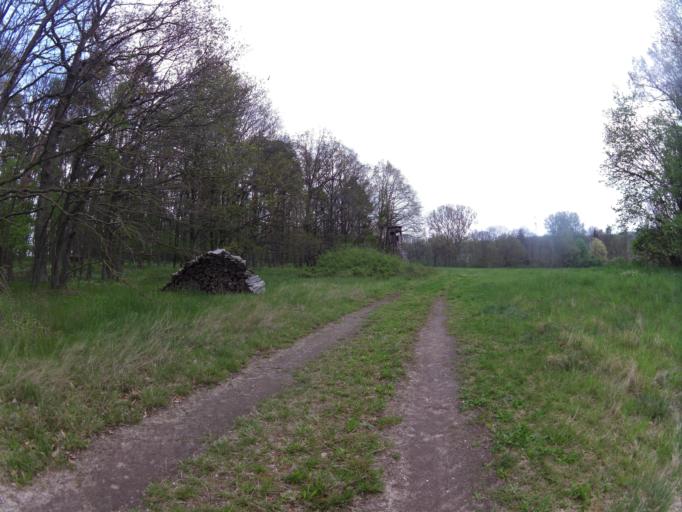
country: DE
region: Bavaria
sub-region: Regierungsbezirk Unterfranken
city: Ochsenfurt
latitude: 49.6997
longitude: 10.0615
